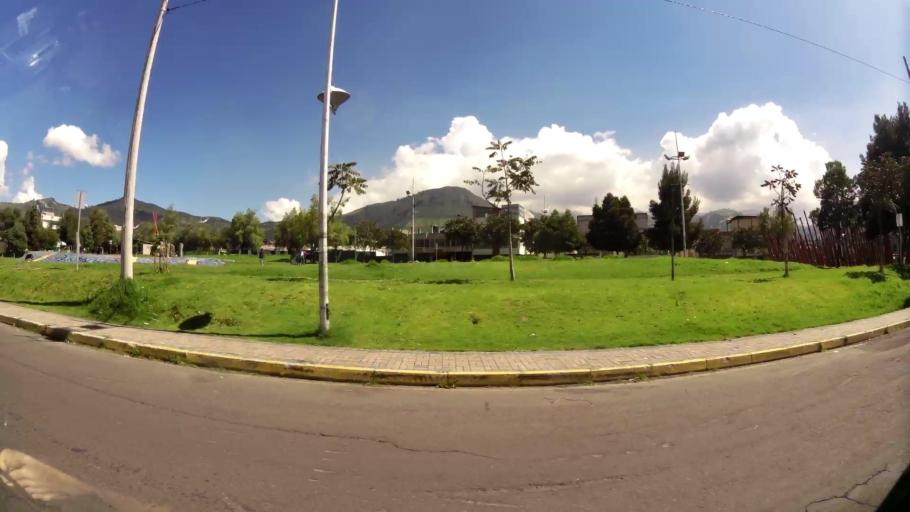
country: EC
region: Pichincha
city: Quito
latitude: -0.2630
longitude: -78.5385
